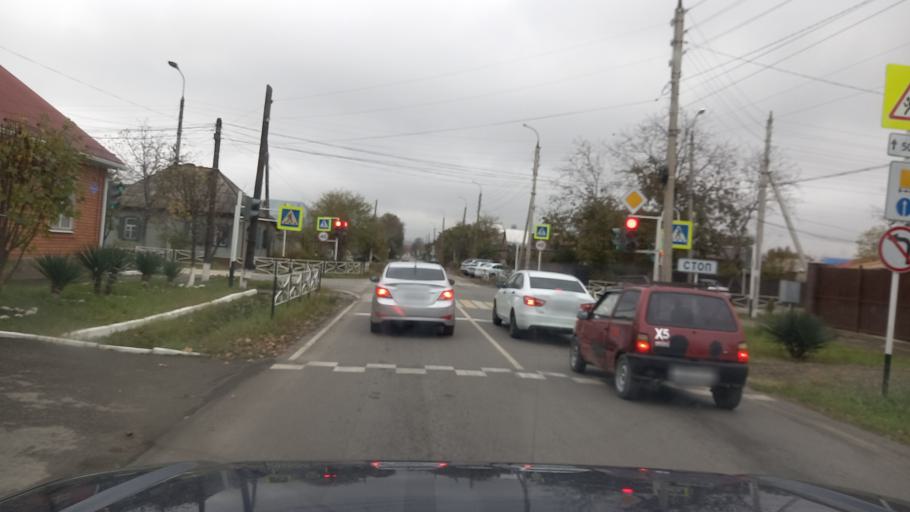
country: RU
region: Adygeya
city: Maykop
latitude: 44.6018
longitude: 40.0806
